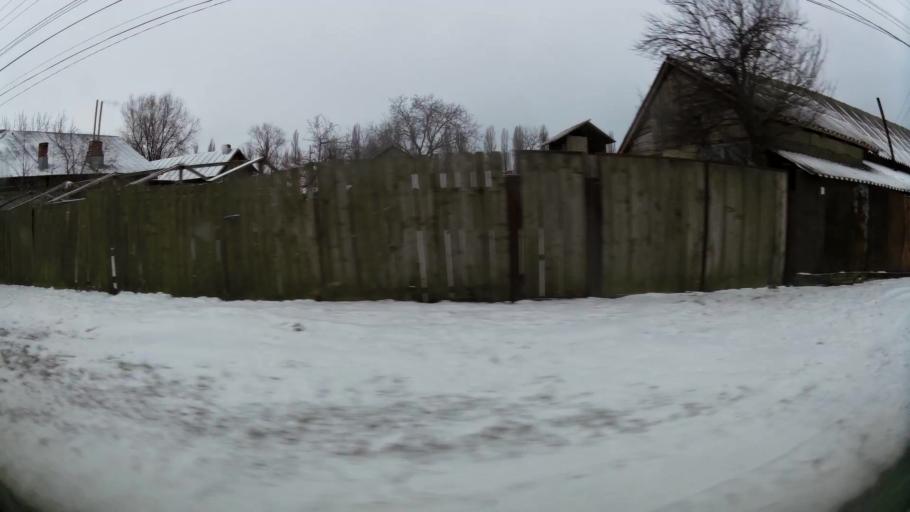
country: RO
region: Prahova
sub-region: Comuna Berceni
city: Corlatesti
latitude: 44.9233
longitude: 26.0749
